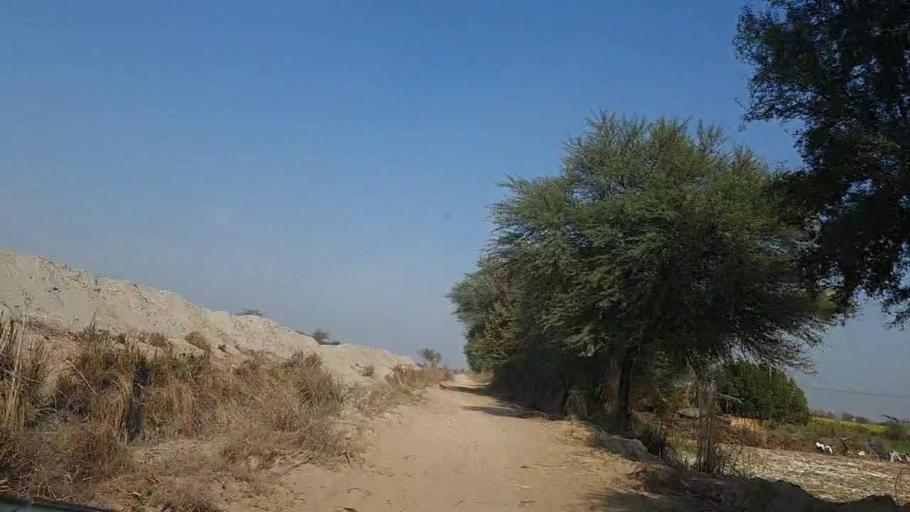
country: PK
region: Sindh
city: Sakrand
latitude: 26.0774
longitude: 68.3583
